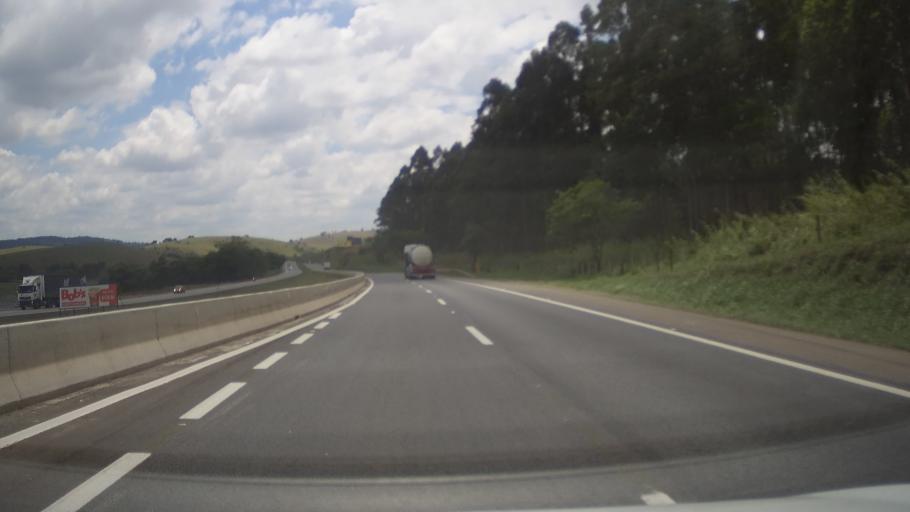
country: BR
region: Minas Gerais
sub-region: Campanha
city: Campanha
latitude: -21.7205
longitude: -45.3789
